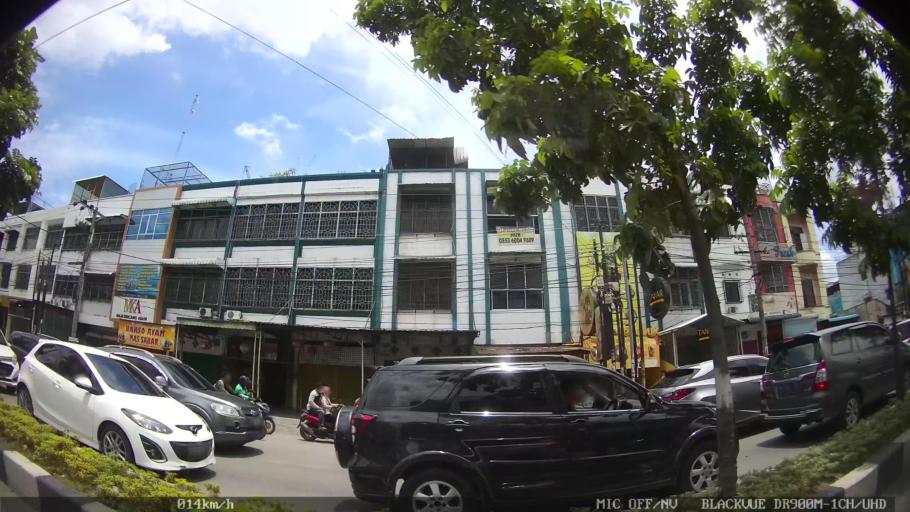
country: ID
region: North Sumatra
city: Medan
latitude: 3.6171
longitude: 98.6809
